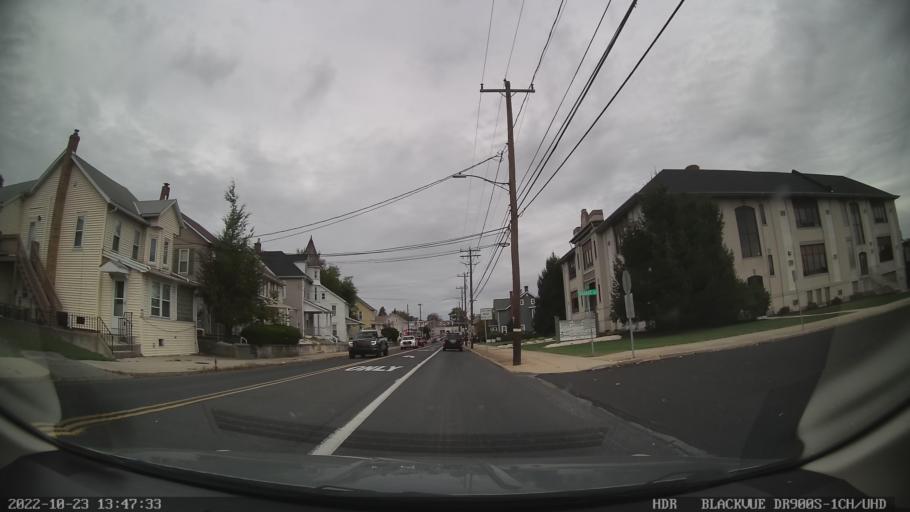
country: US
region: Pennsylvania
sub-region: Lehigh County
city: Fullerton
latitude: 40.6353
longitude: -75.4707
